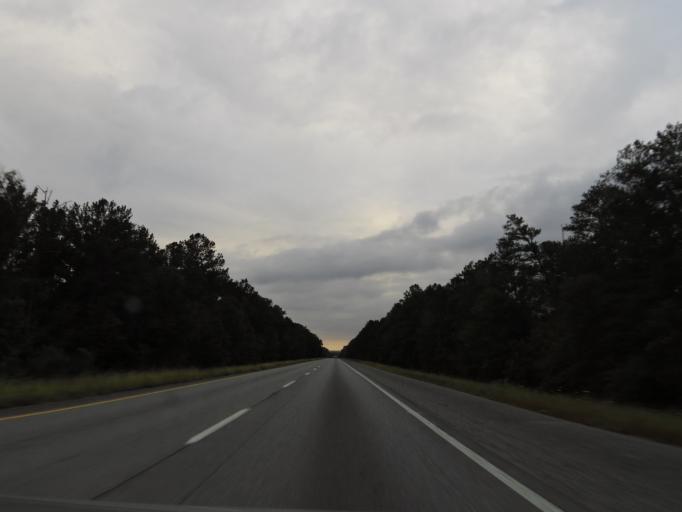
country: US
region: Alabama
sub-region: Saint Clair County
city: Ashville
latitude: 33.8220
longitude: -86.3449
